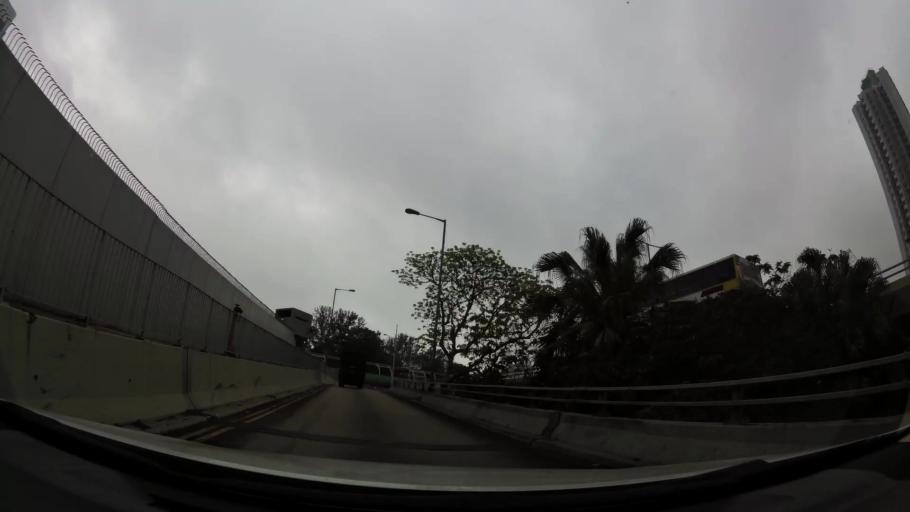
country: HK
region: Central and Western
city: Central
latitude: 22.2480
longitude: 114.1609
